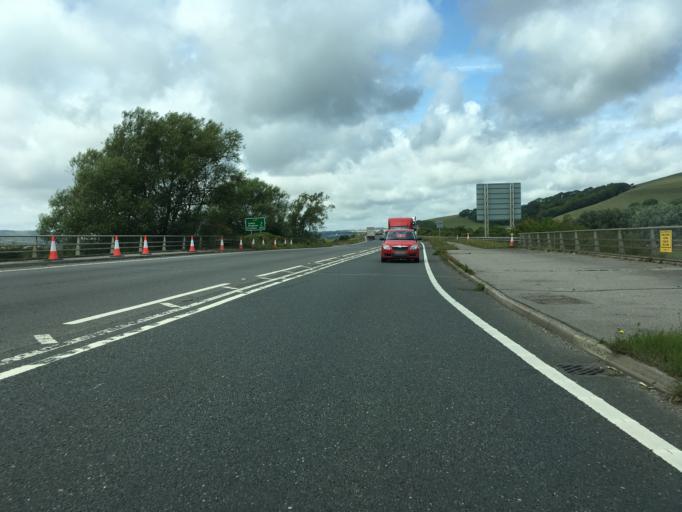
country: GB
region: England
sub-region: East Sussex
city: Ringmer
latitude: 50.8545
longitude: 0.0509
